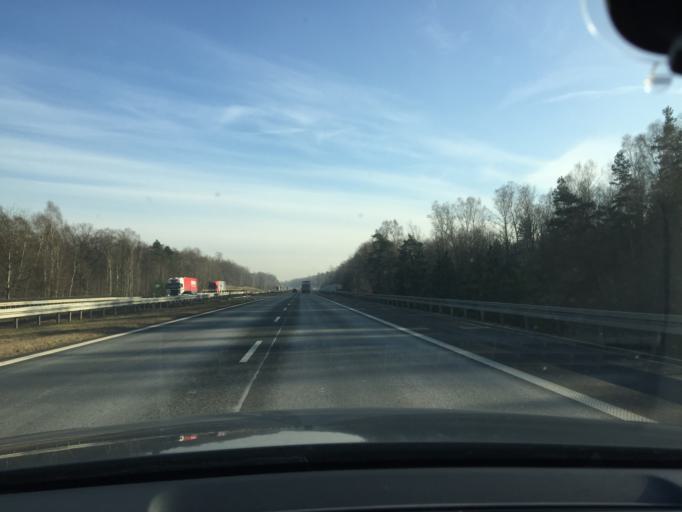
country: PL
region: Silesian Voivodeship
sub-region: Katowice
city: Murcki
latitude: 50.2254
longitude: 19.0842
